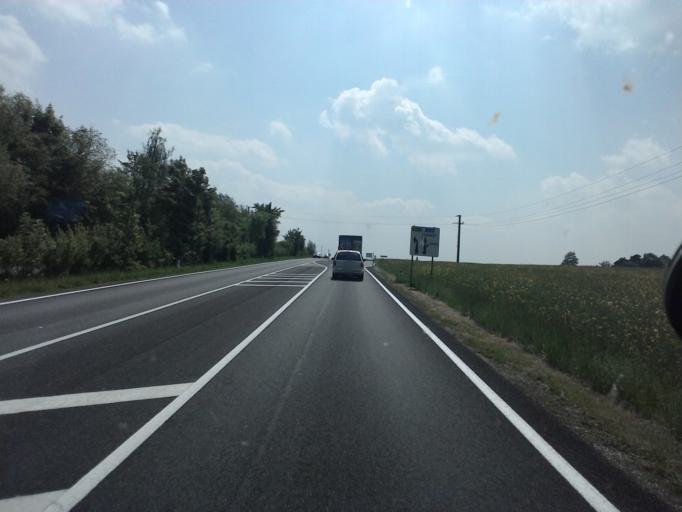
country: AT
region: Upper Austria
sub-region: Politischer Bezirk Steyr-Land
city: Sierning
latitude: 48.0473
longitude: 14.3239
